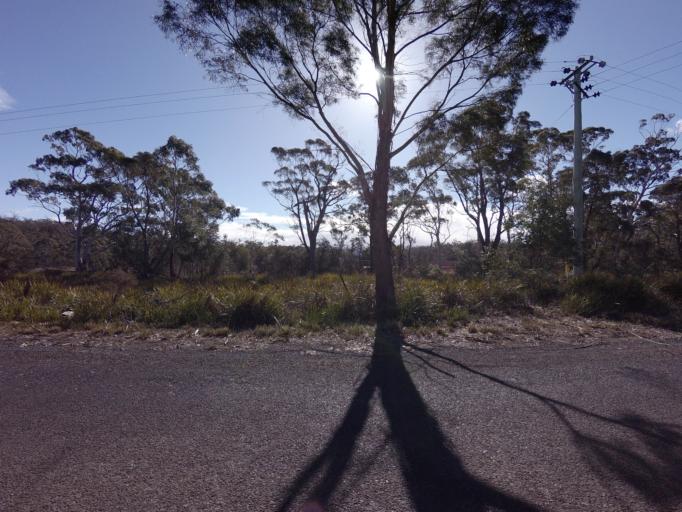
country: AU
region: Tasmania
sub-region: Sorell
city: Sorell
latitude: -42.3575
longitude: 147.9631
